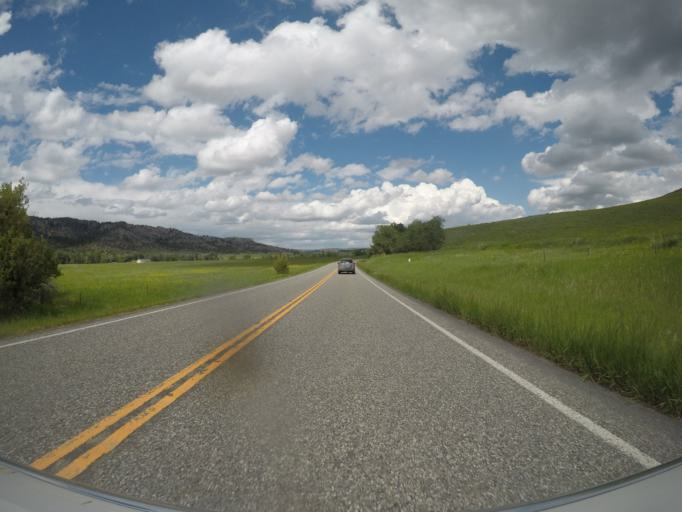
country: US
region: Montana
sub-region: Sweet Grass County
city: Big Timber
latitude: 45.6930
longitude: -110.0385
